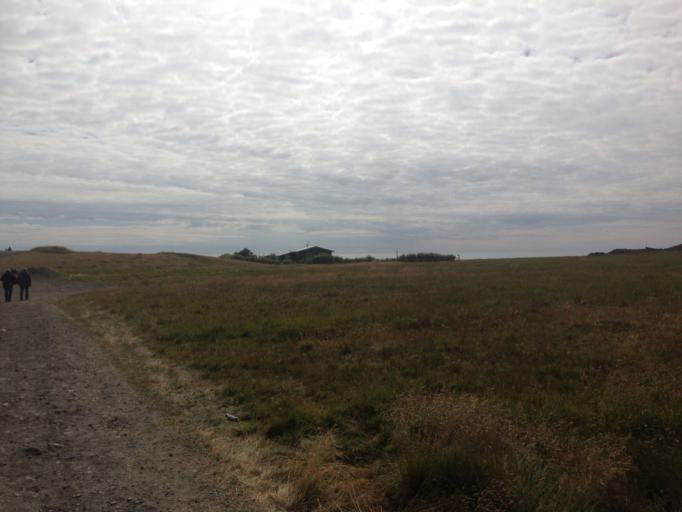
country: IS
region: West
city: Olafsvik
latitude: 64.7662
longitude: -23.6284
